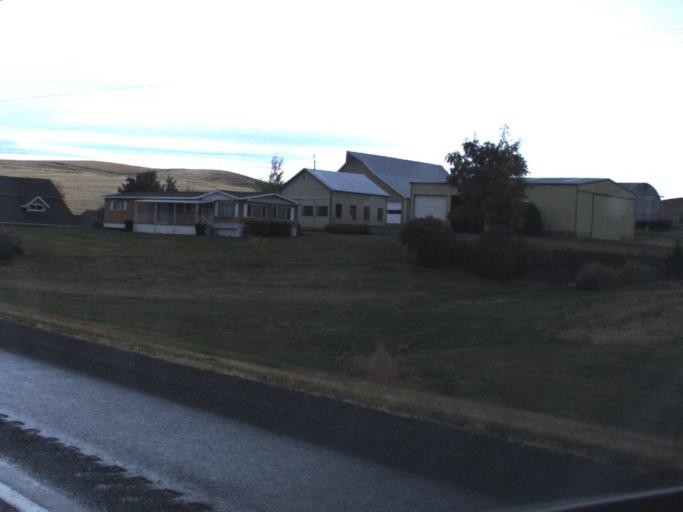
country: US
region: Washington
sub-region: Asotin County
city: Clarkston
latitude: 46.5531
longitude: -117.1025
